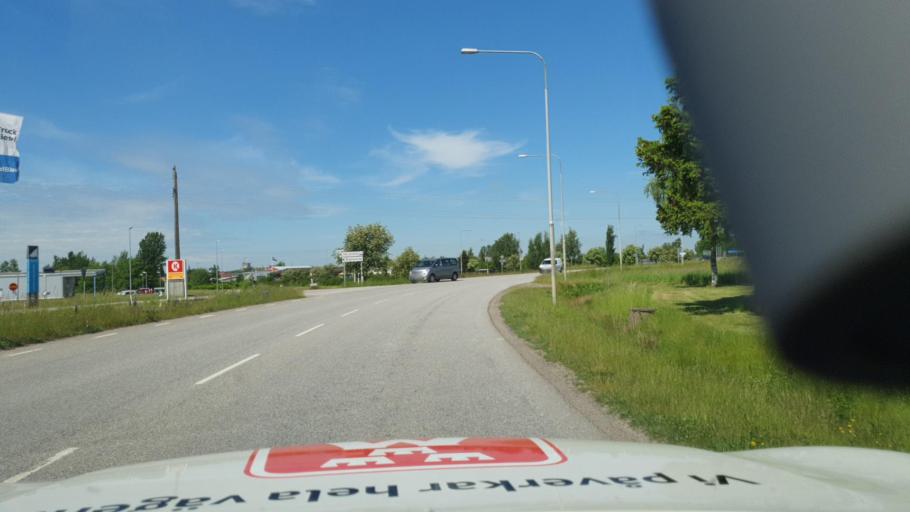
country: SE
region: Vaestra Goetaland
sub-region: Vara Kommun
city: Vara
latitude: 58.2543
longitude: 12.9727
